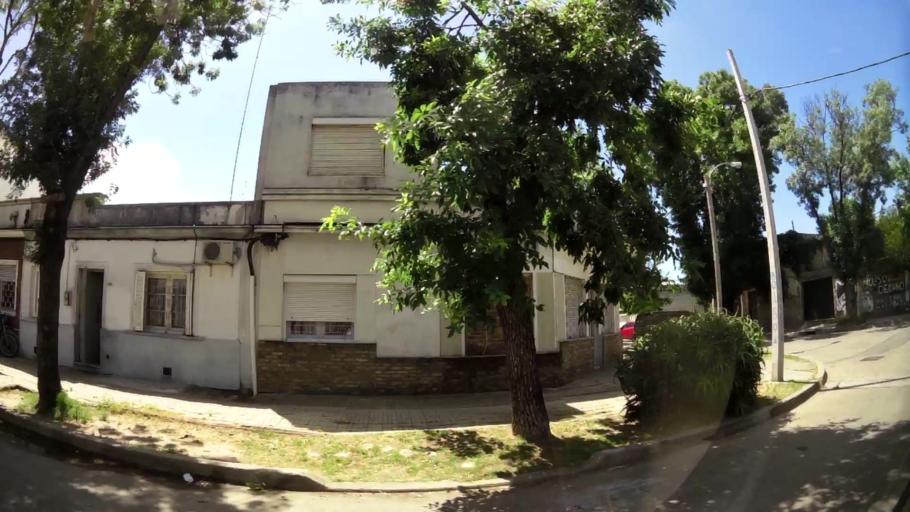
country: UY
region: Montevideo
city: Montevideo
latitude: -34.8684
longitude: -56.1776
